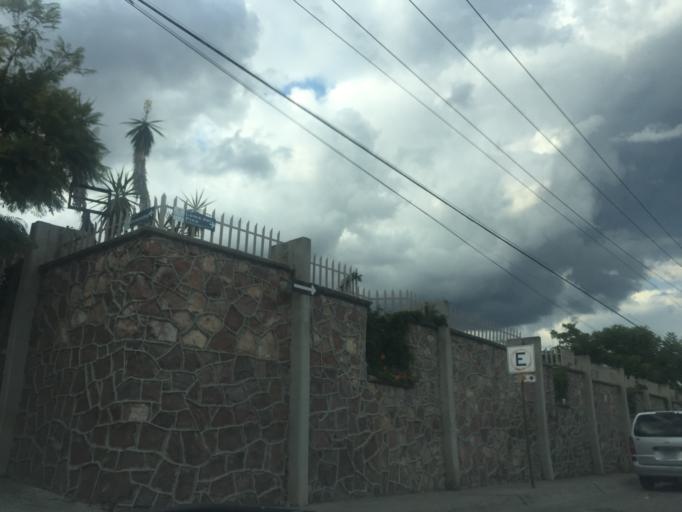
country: MX
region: Guanajuato
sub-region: Leon
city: La Ermita
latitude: 21.1504
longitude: -101.7102
